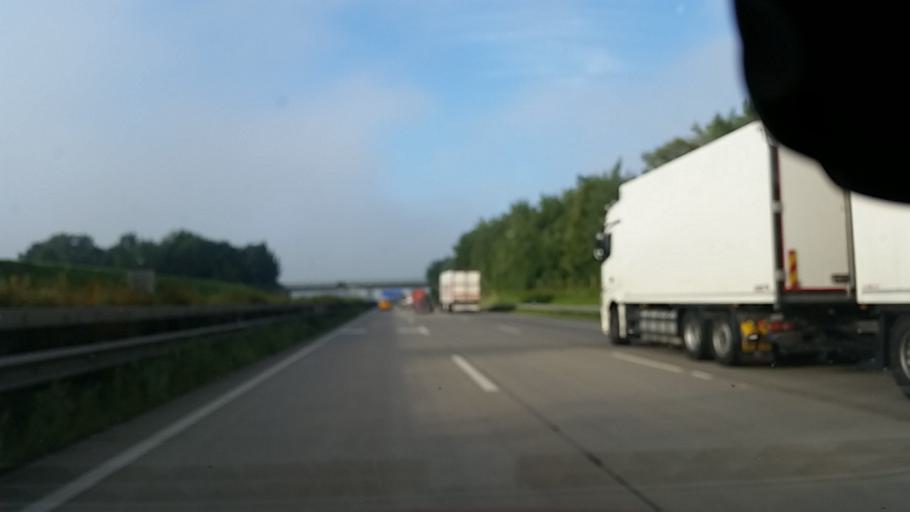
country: DE
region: Lower Saxony
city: Buehren
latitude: 52.8272
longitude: 8.2145
